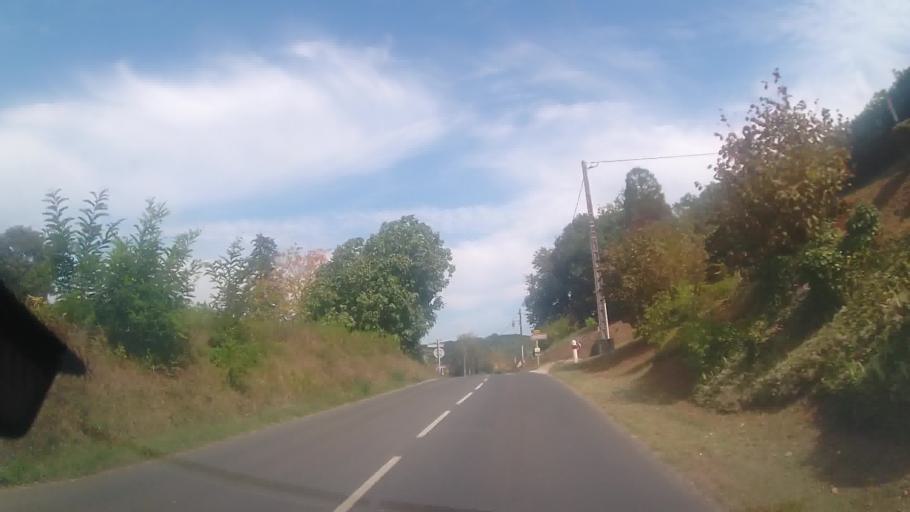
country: FR
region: Aquitaine
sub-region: Departement de la Dordogne
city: Carsac-Aillac
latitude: 44.8274
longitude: 1.3049
